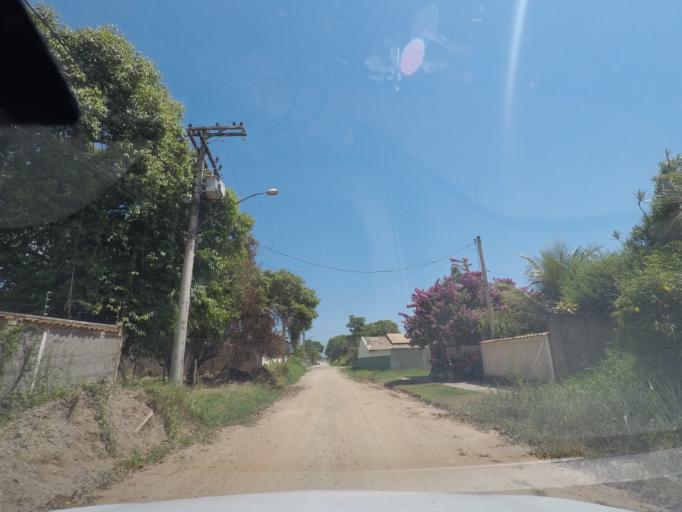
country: BR
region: Rio de Janeiro
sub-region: Marica
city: Marica
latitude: -22.9537
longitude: -42.9559
